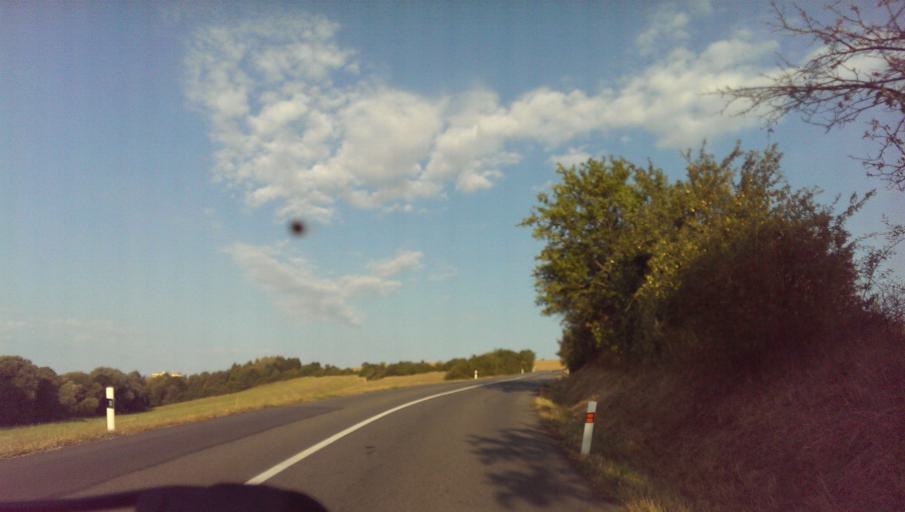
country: CZ
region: South Moravian
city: Domanin
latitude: 49.0527
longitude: 17.2841
